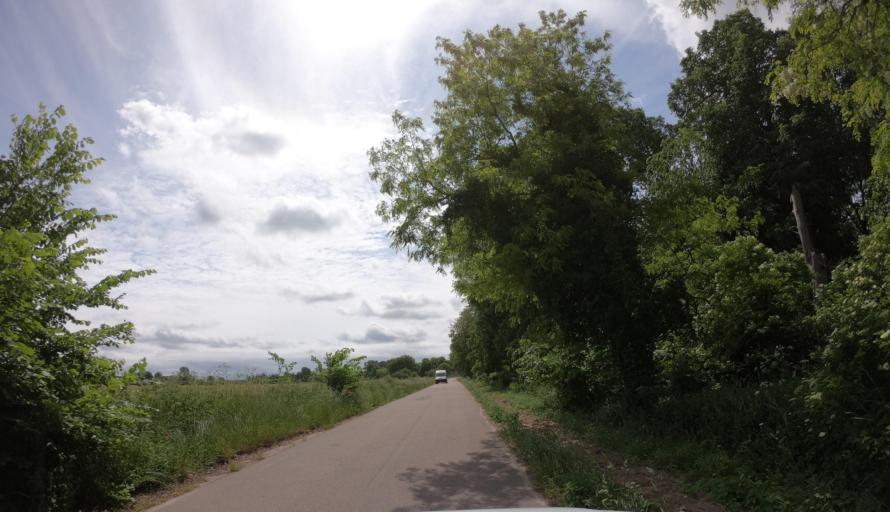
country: PL
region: West Pomeranian Voivodeship
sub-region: Powiat kamienski
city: Wolin
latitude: 53.8279
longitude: 14.7080
